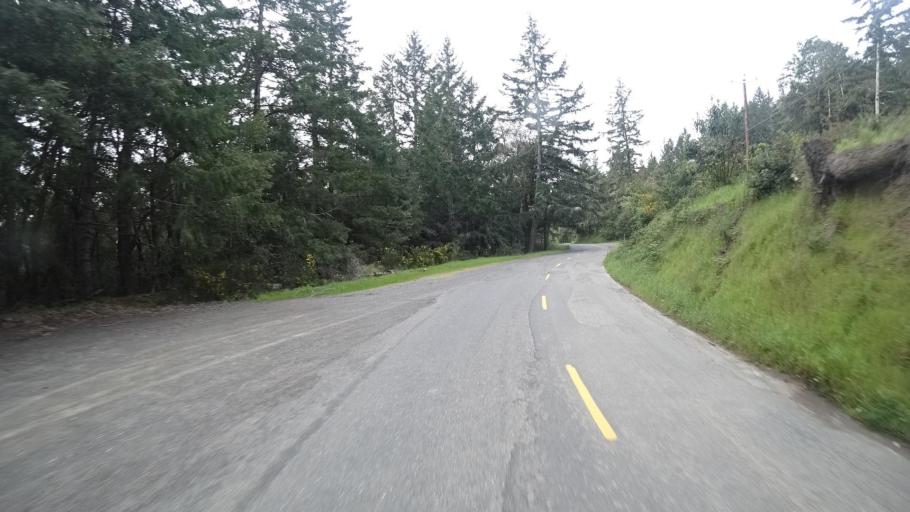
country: US
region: California
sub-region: Humboldt County
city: Redway
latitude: 40.3033
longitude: -123.8214
